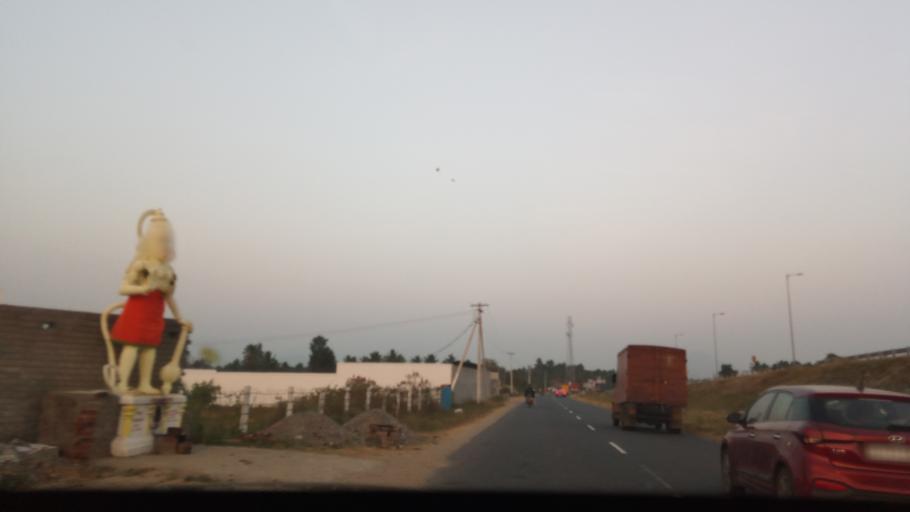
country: IN
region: Tamil Nadu
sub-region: Salem
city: Salem
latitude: 11.6632
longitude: 78.2310
